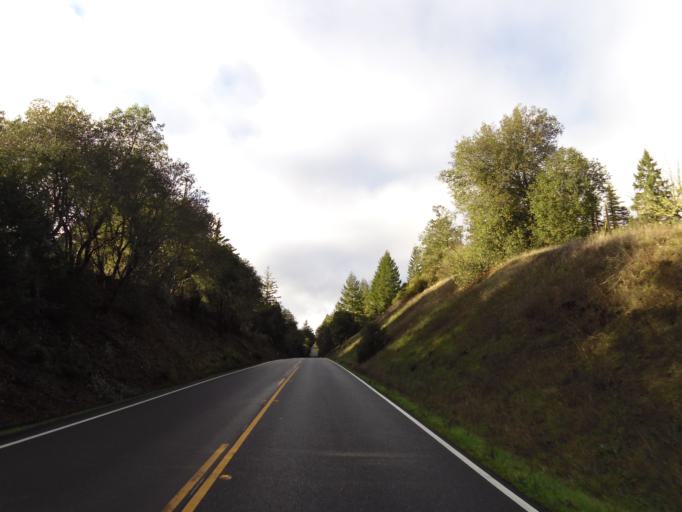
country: US
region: California
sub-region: Mendocino County
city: Boonville
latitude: 39.1037
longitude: -123.4942
